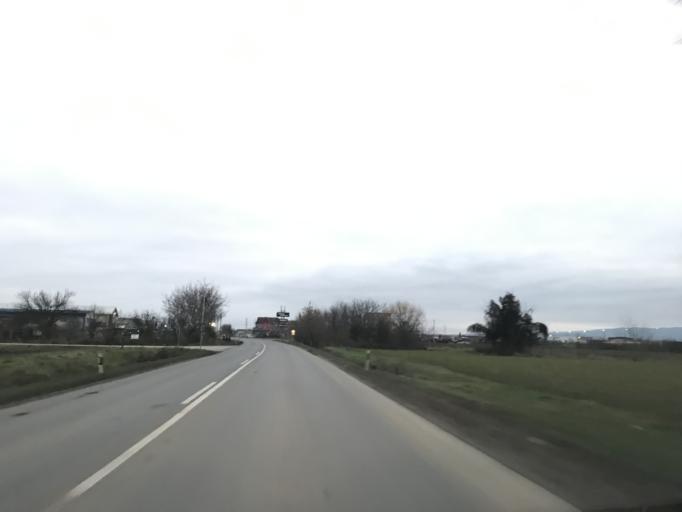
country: RS
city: Rumenka
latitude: 45.2842
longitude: 19.7667
